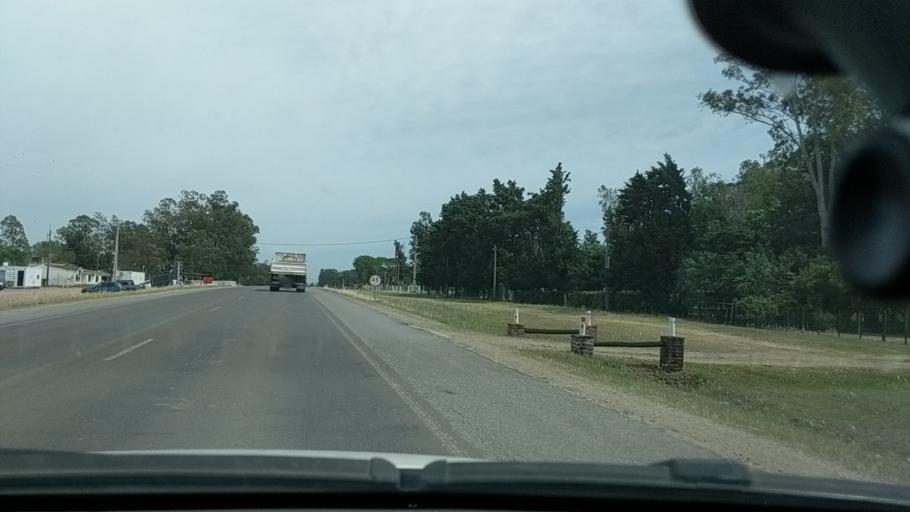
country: UY
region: Durazno
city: Durazno
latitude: -33.4189
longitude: -56.5050
